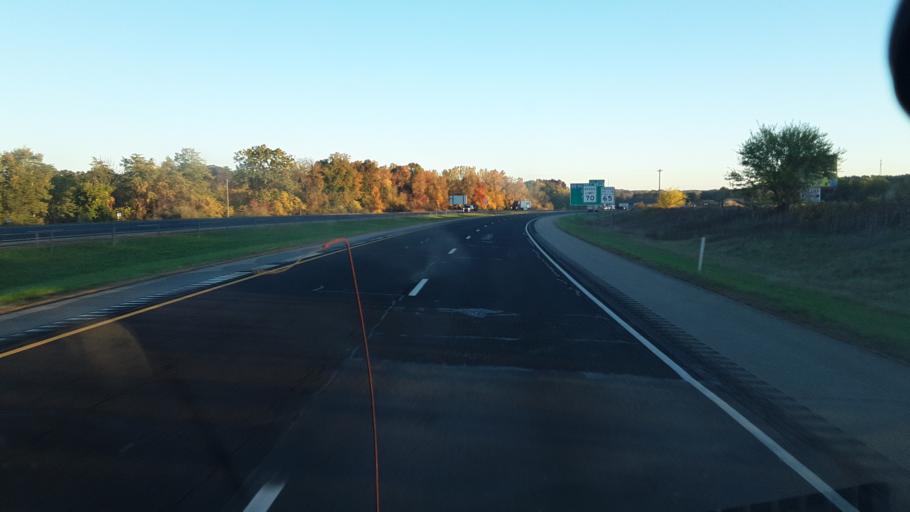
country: US
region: Indiana
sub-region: Steuben County
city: Fremont
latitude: 41.7142
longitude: -85.0040
